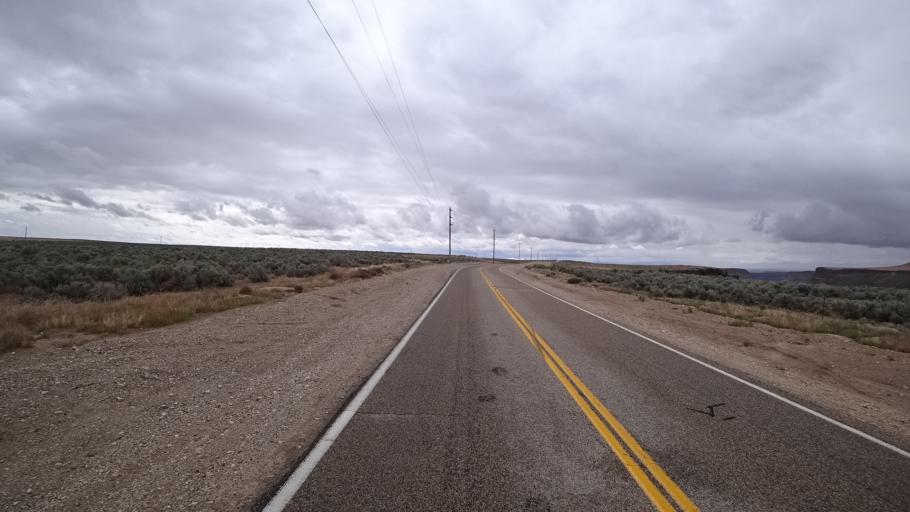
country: US
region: Idaho
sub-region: Owyhee County
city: Murphy
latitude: 43.2512
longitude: -116.3725
